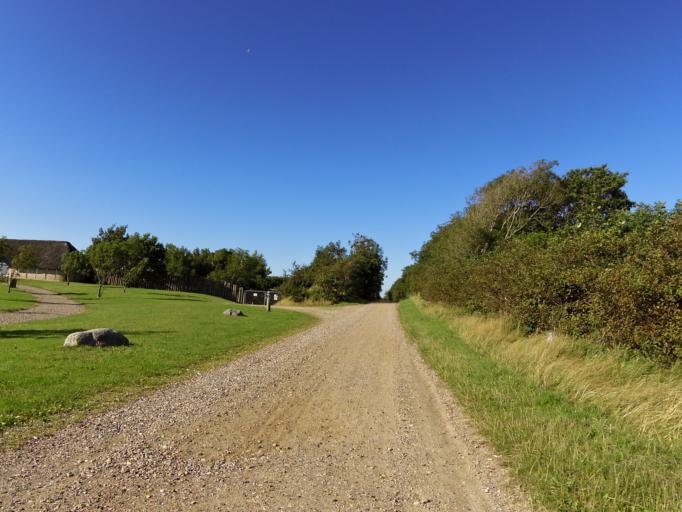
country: DK
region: South Denmark
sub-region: Tonder Kommune
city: Sherrebek
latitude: 55.1522
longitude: 8.7422
